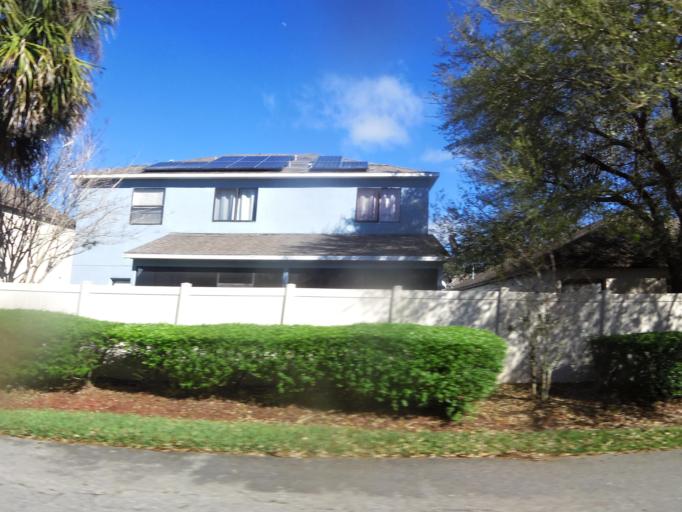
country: US
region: Florida
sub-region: Brevard County
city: Titusville
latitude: 28.5448
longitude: -80.8062
